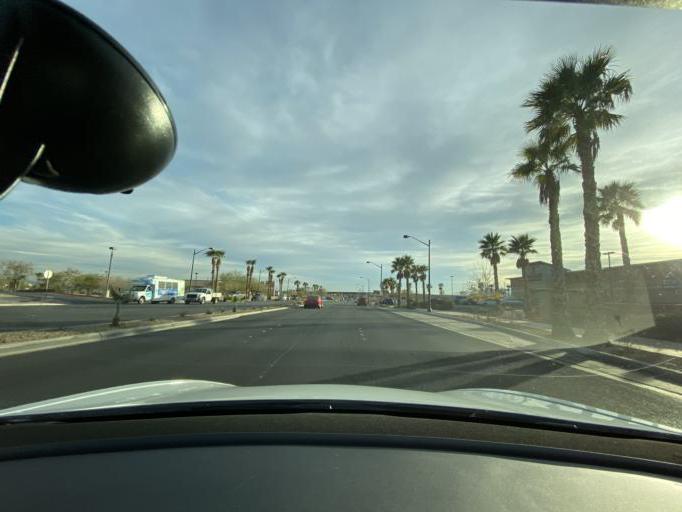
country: US
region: Nevada
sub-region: Clark County
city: Summerlin South
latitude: 36.2839
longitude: -115.2880
